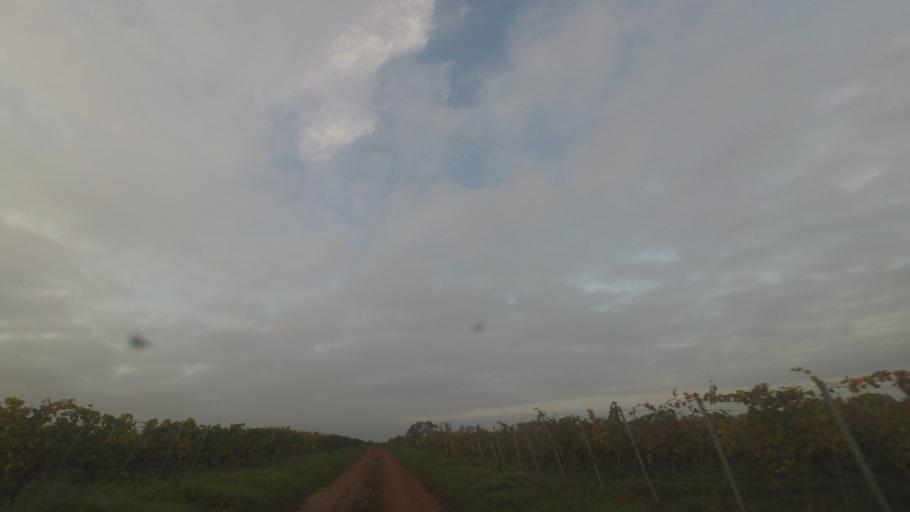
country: DE
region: Rheinland-Pfalz
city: Offstein
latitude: 49.5984
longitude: 8.2561
